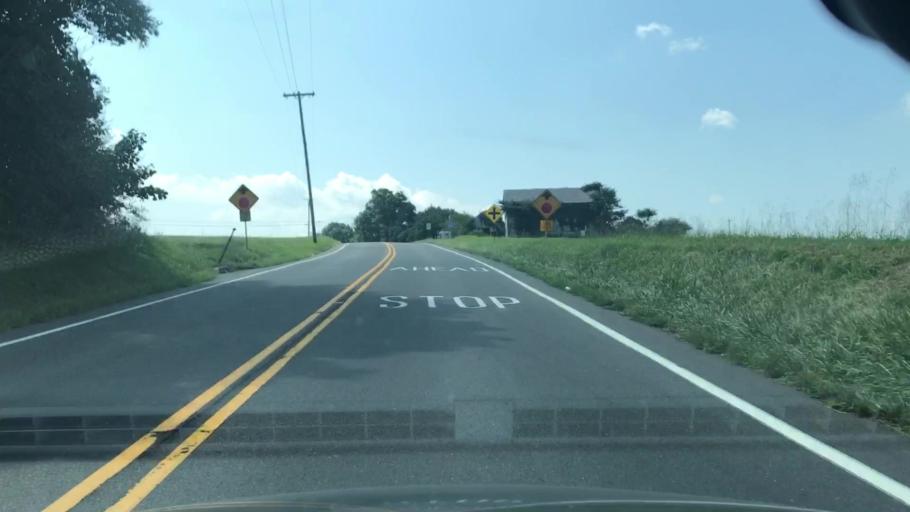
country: US
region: New Jersey
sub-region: Hunterdon County
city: Milford
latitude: 40.6263
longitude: -75.0375
